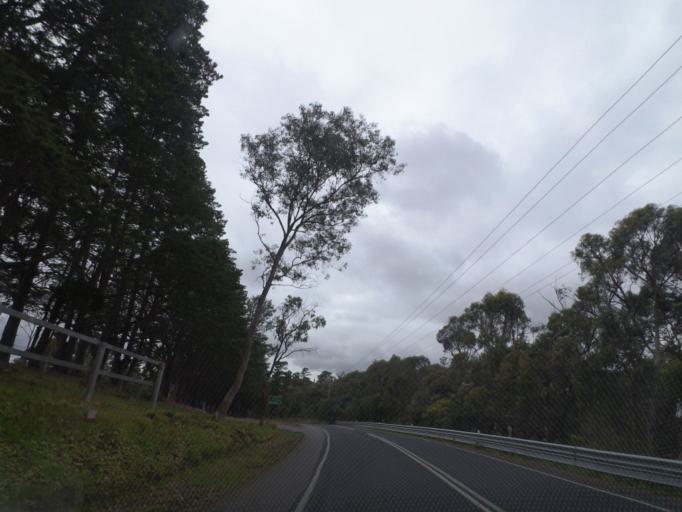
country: AU
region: Victoria
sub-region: Nillumbik
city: Hurstbridge
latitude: -37.6450
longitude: 145.2331
